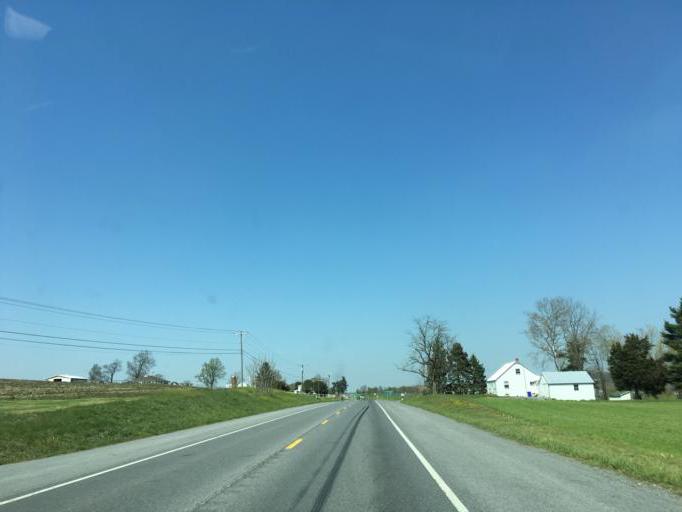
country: US
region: Maryland
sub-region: Frederick County
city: Woodsboro
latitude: 39.5110
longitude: -77.3207
